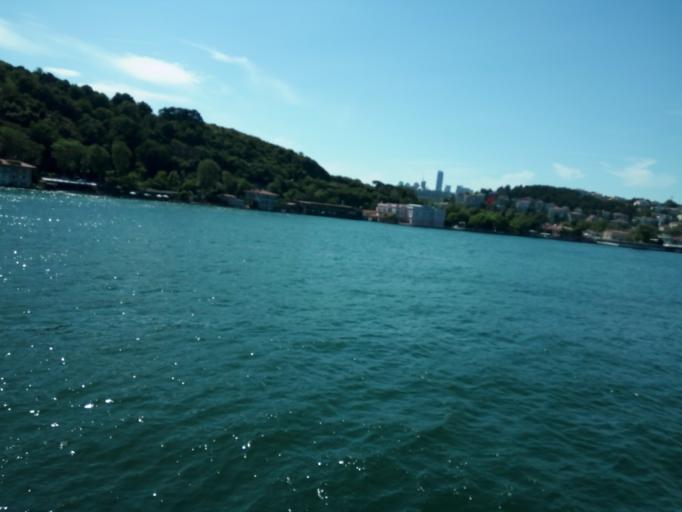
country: TR
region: Istanbul
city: Sisli
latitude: 41.0935
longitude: 29.0579
